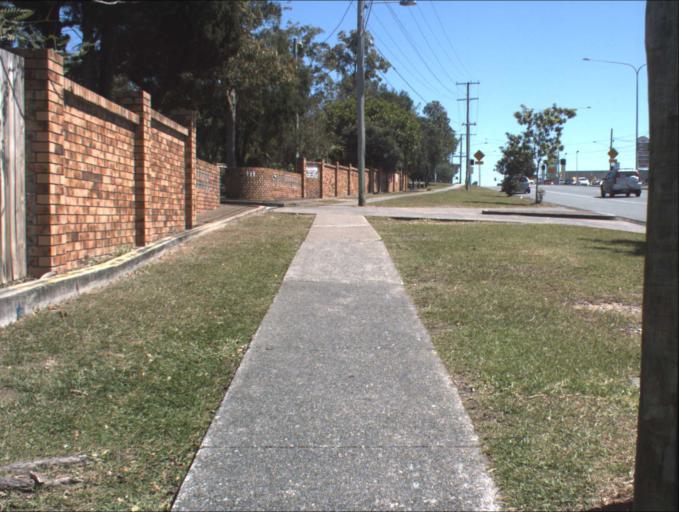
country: AU
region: Queensland
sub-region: Logan
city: Logan City
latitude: -27.6279
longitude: 153.1180
